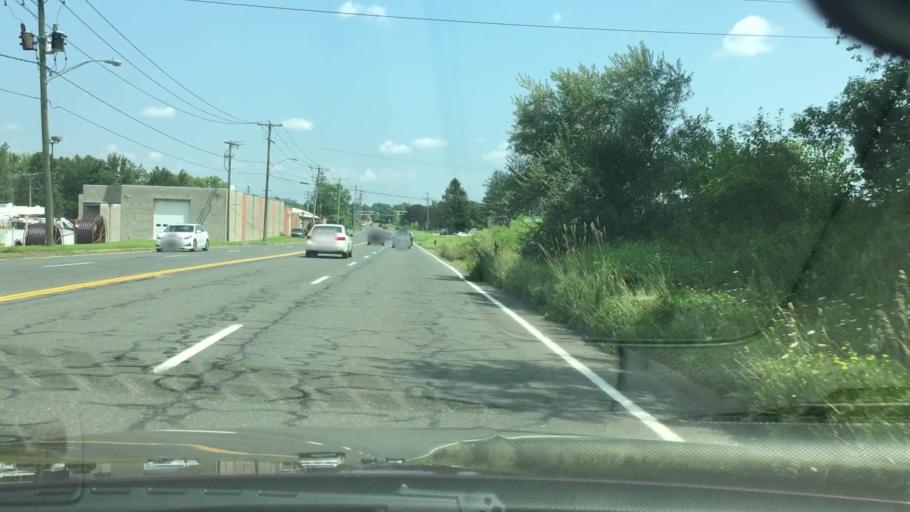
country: US
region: Connecticut
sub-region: Hartford County
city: East Hartford
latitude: 41.7943
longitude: -72.5665
